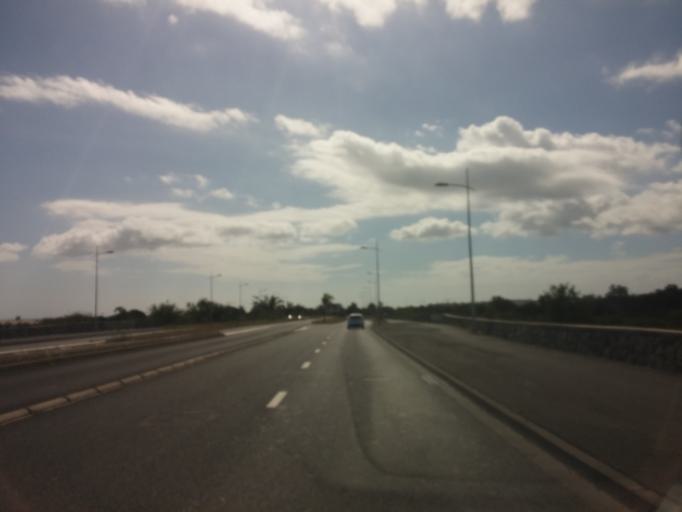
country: RE
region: Reunion
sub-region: Reunion
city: Le Port
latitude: -20.9558
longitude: 55.2942
